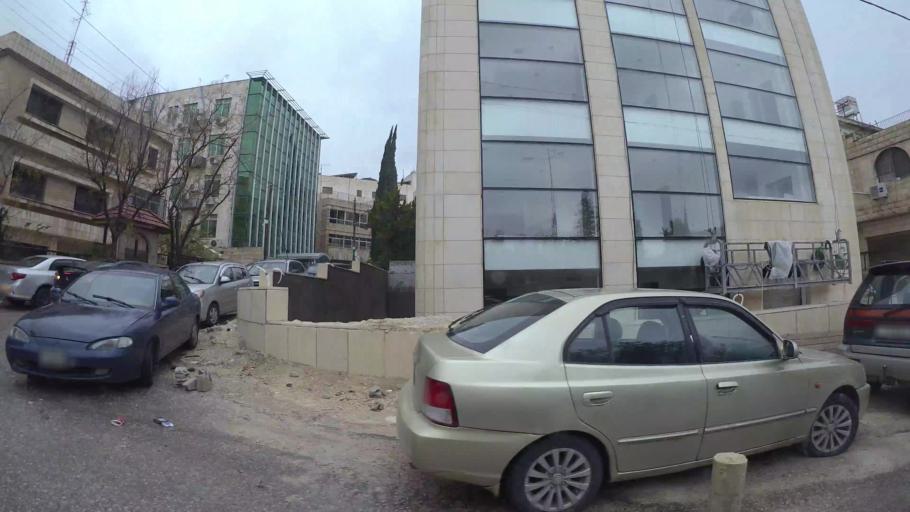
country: JO
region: Amman
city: Amman
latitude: 31.9611
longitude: 35.9007
